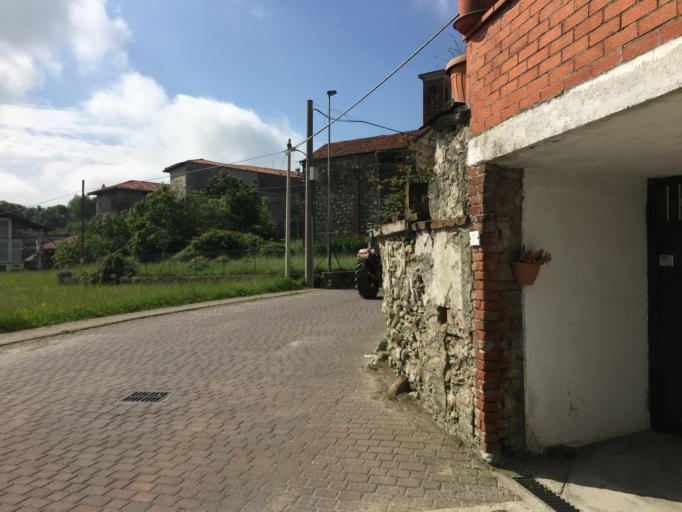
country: IT
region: Piedmont
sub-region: Provincia di Torino
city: Vialfre
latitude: 45.3823
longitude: 7.8180
